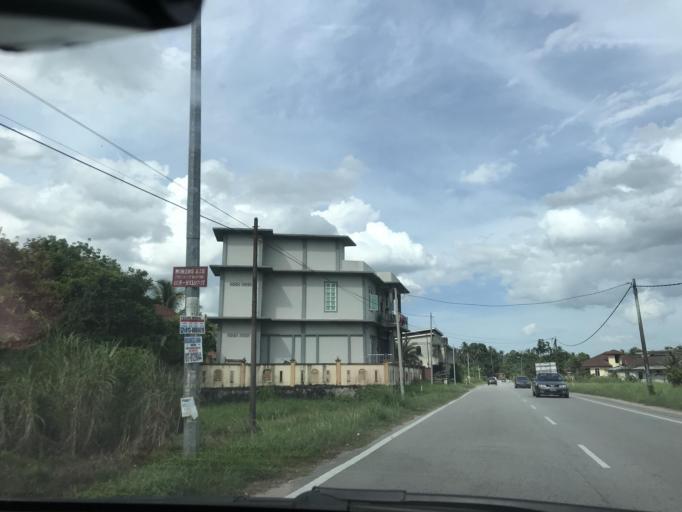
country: MY
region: Kelantan
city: Kampung Lemal
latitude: 6.0335
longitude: 102.1621
